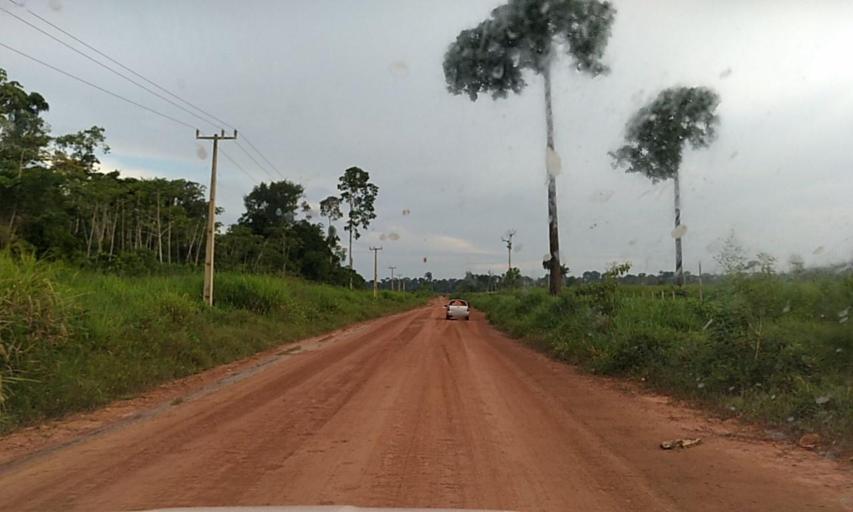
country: BR
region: Para
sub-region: Senador Jose Porfirio
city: Senador Jose Porfirio
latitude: -2.6885
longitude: -51.8270
